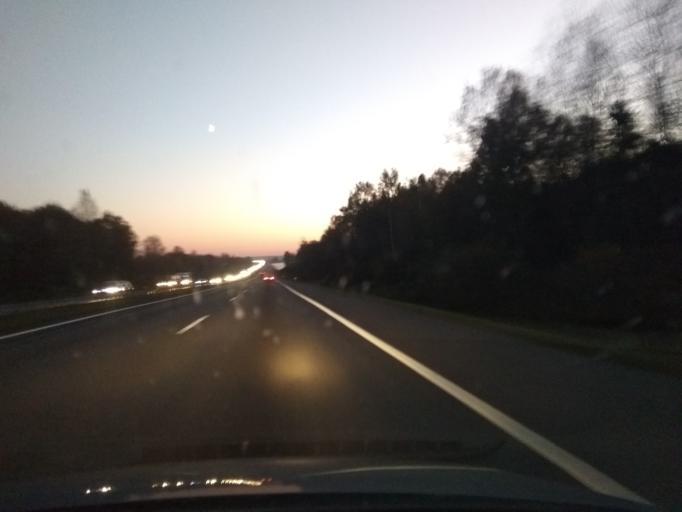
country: BY
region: Minsk
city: Enyerhyetykaw
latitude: 53.6326
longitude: 27.0609
